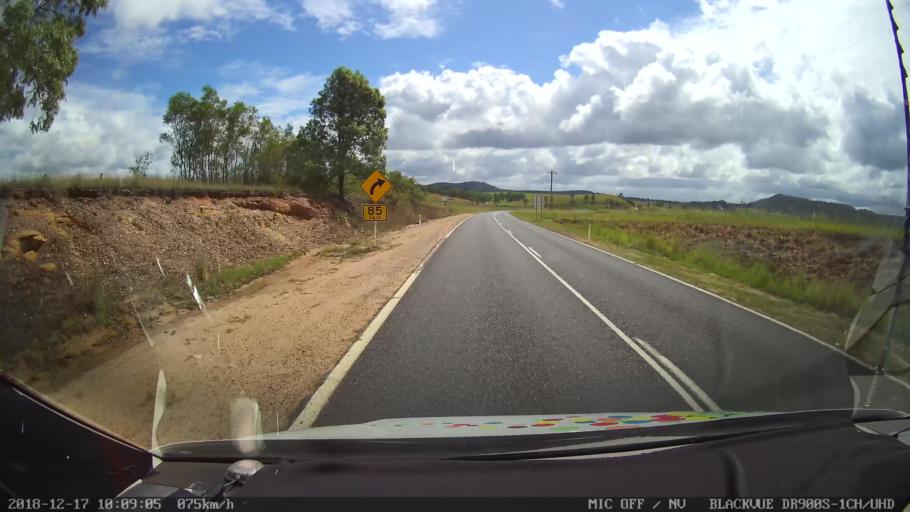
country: AU
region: New South Wales
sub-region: Tenterfield Municipality
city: Carrolls Creek
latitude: -28.8883
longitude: 152.5393
